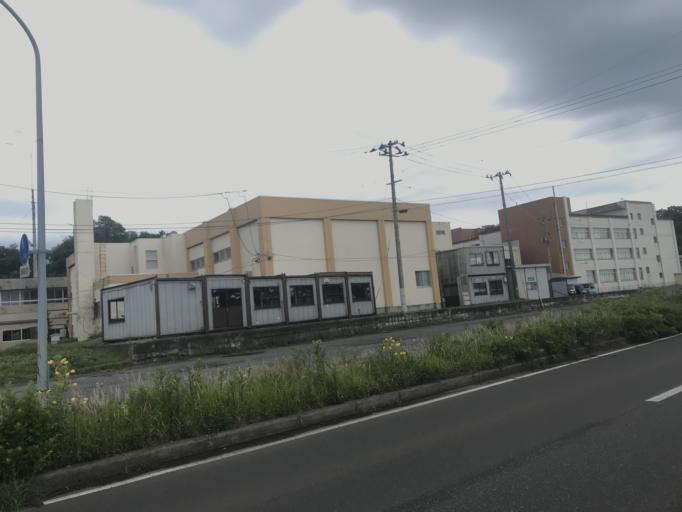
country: JP
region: Aomori
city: Shimokizukuri
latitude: 40.7799
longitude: 140.2101
